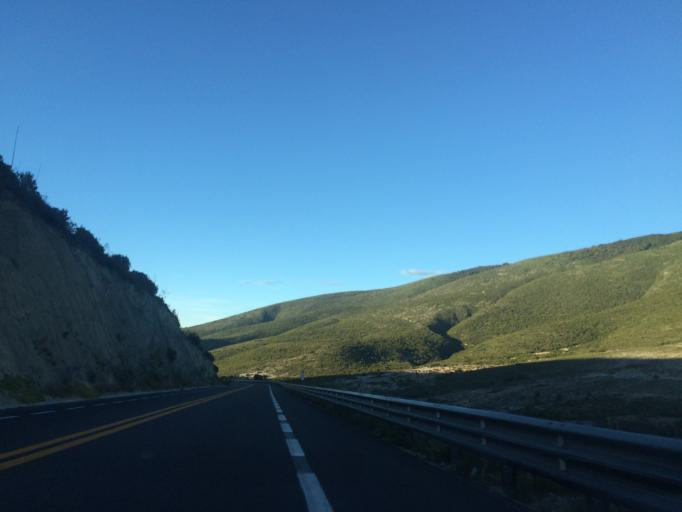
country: MX
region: Puebla
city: Morelos Canada
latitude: 18.6787
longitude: -97.4603
